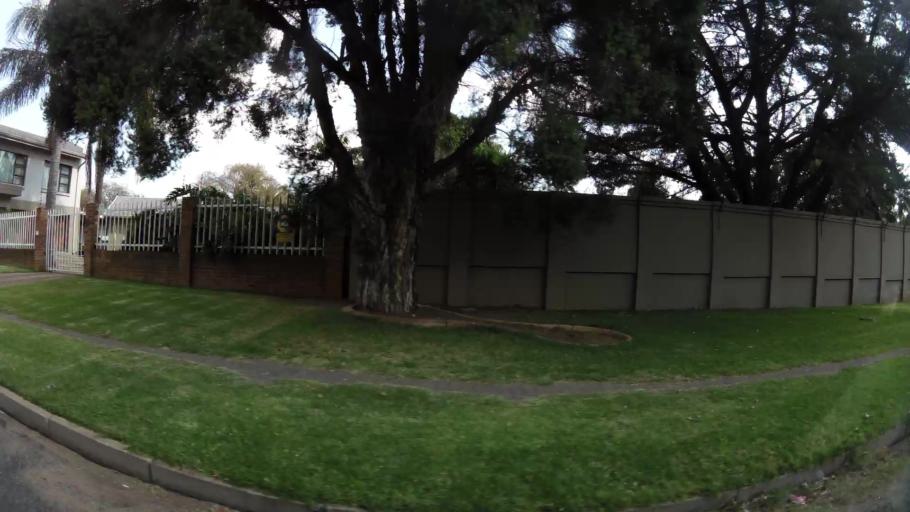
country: ZA
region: Gauteng
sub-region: City of Johannesburg Metropolitan Municipality
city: Modderfontein
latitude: -26.0850
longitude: 28.2347
